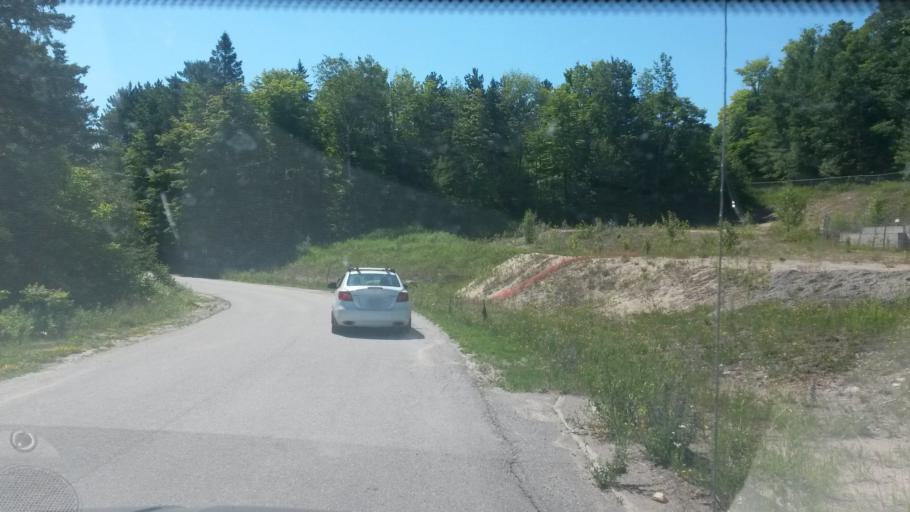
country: CA
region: Ontario
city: Barrie
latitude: 44.5532
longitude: -79.6810
